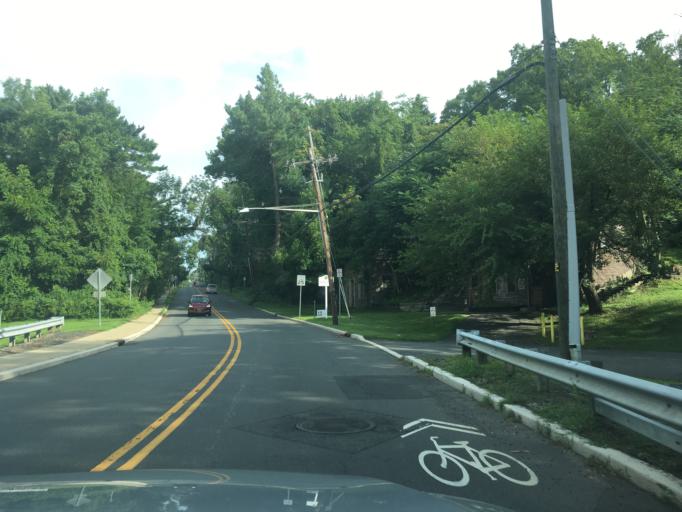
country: US
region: New Jersey
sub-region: Mercer County
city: Princeton
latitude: 40.3437
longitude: -74.6378
